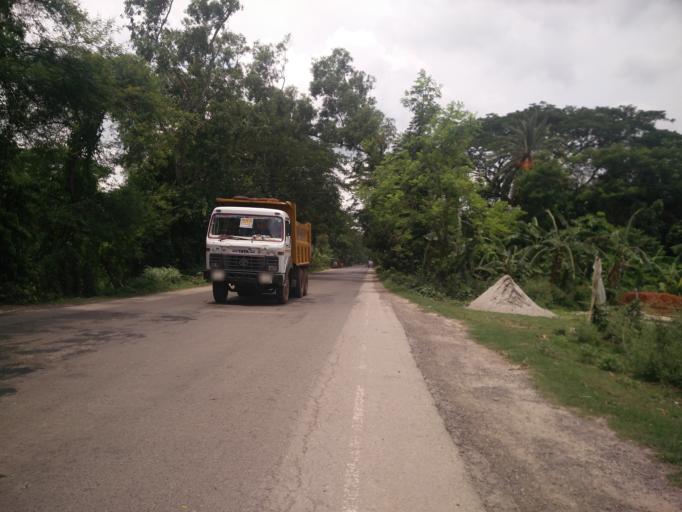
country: BD
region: Khulna
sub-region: Magura
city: Magura
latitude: 23.5449
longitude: 89.5292
